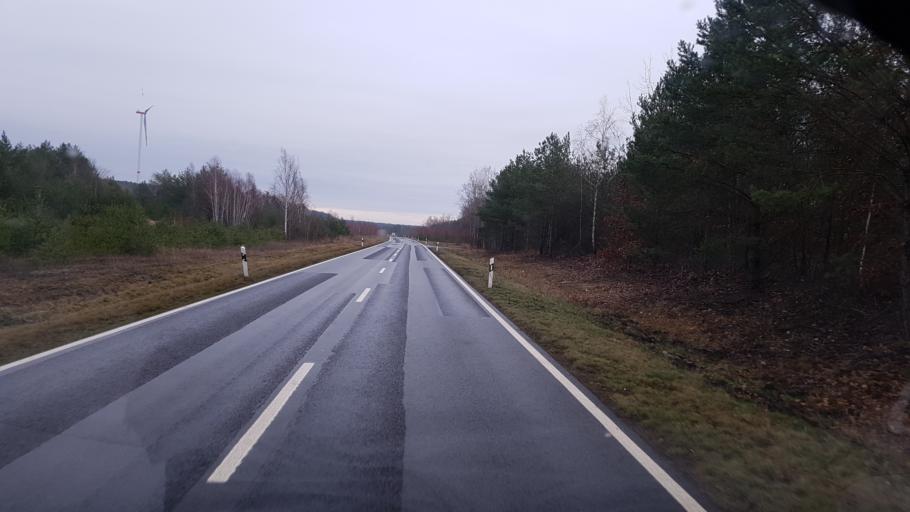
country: DE
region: Brandenburg
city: Schwarzheide
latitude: 51.5153
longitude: 13.8411
